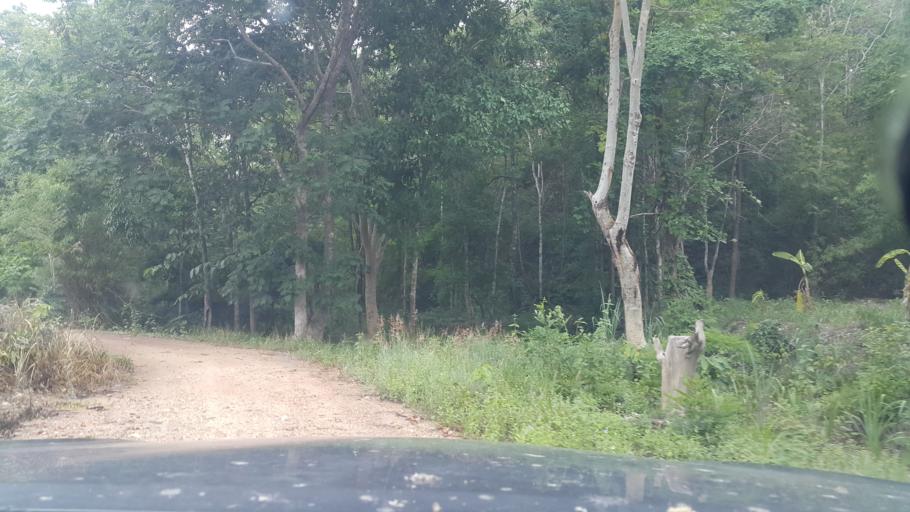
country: TH
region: Chiang Mai
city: Hang Dong
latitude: 18.6865
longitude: 98.8429
